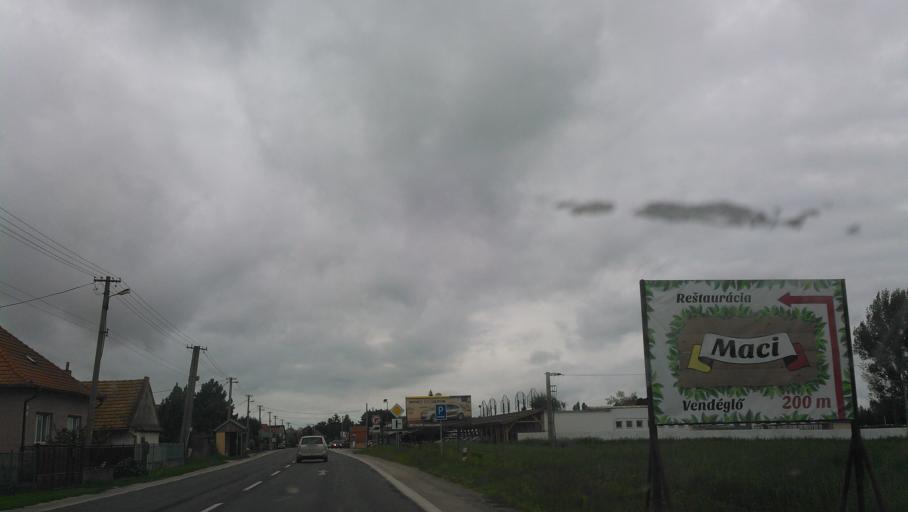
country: SK
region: Trnavsky
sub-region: Okres Dunajska Streda
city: Velky Meder
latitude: 47.9386
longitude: 17.7179
